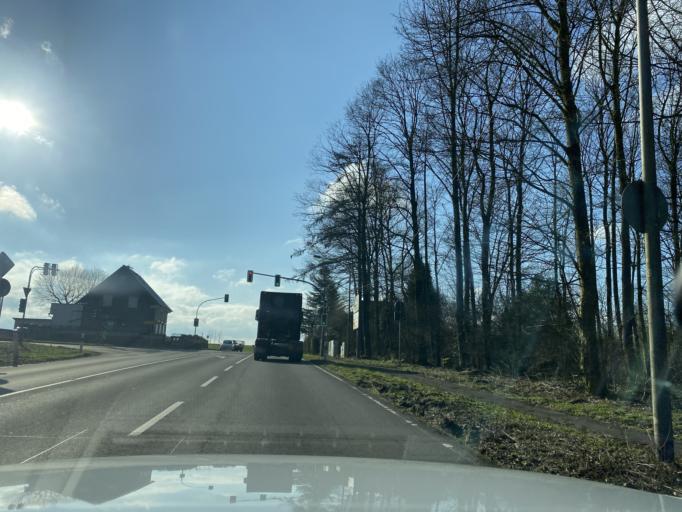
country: DE
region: North Rhine-Westphalia
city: Wermelskirchen
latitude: 51.1678
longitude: 7.2651
